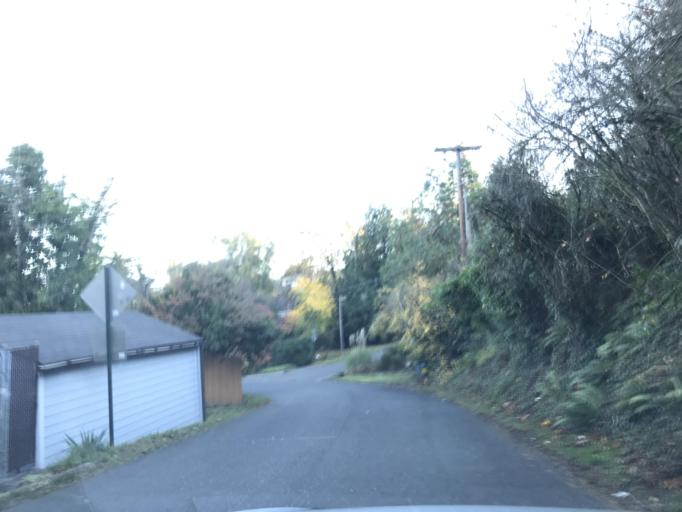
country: US
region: Washington
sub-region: Whatcom County
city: Geneva
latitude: 48.7550
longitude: -122.4142
